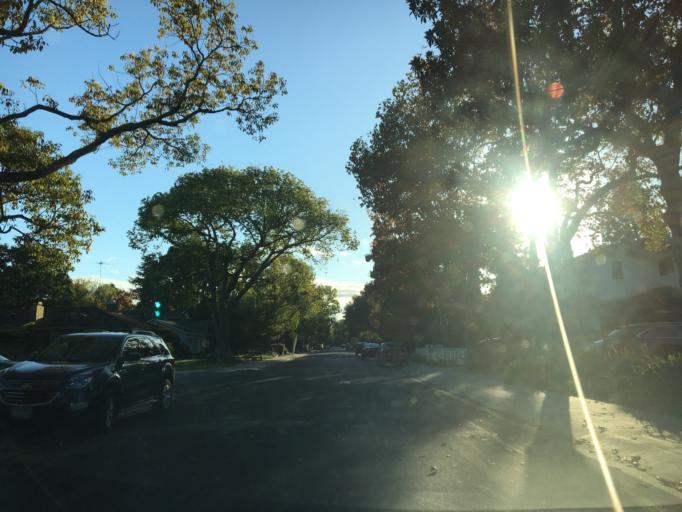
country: US
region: California
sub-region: Santa Clara County
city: Palo Alto
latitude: 37.4338
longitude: -122.1329
